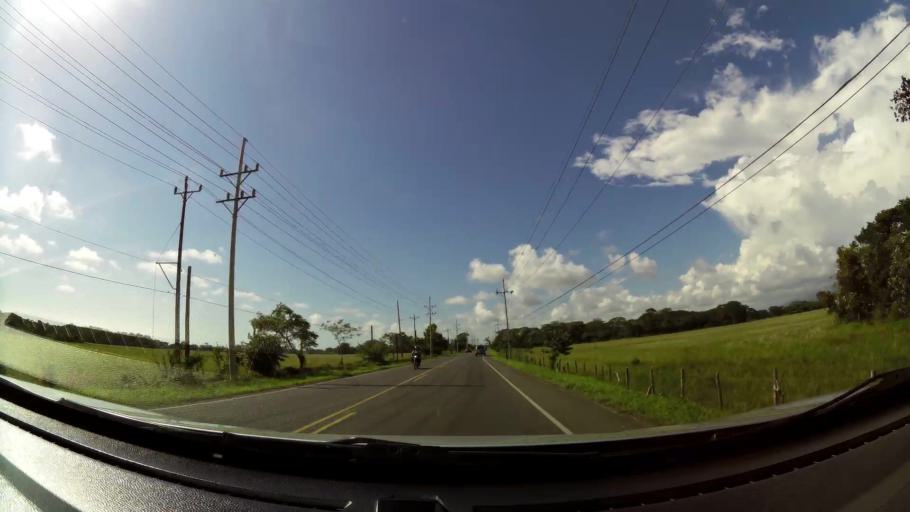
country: CR
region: Puntarenas
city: Quepos
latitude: 9.4525
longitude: -84.1699
